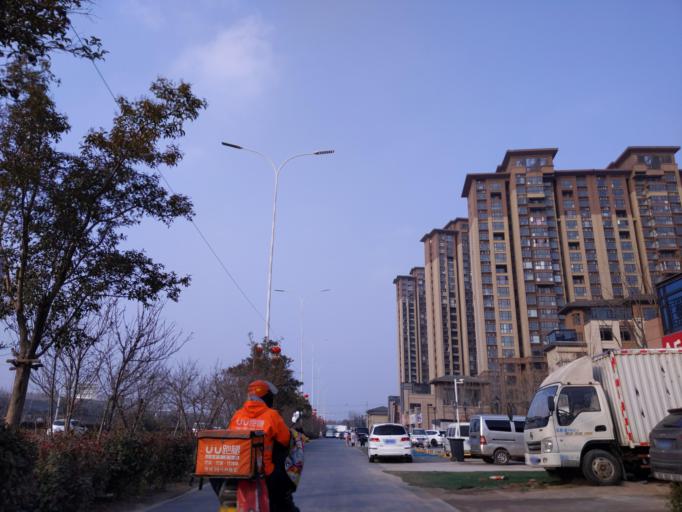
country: CN
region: Henan Sheng
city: Puyang
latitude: 35.8143
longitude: 115.0226
